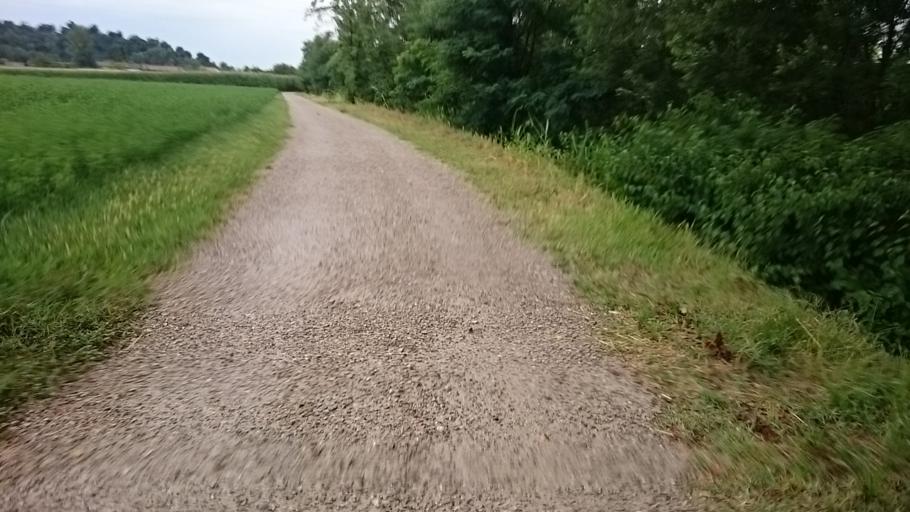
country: IT
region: Veneto
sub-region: Provincia di Treviso
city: One
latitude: 45.7988
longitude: 11.8929
